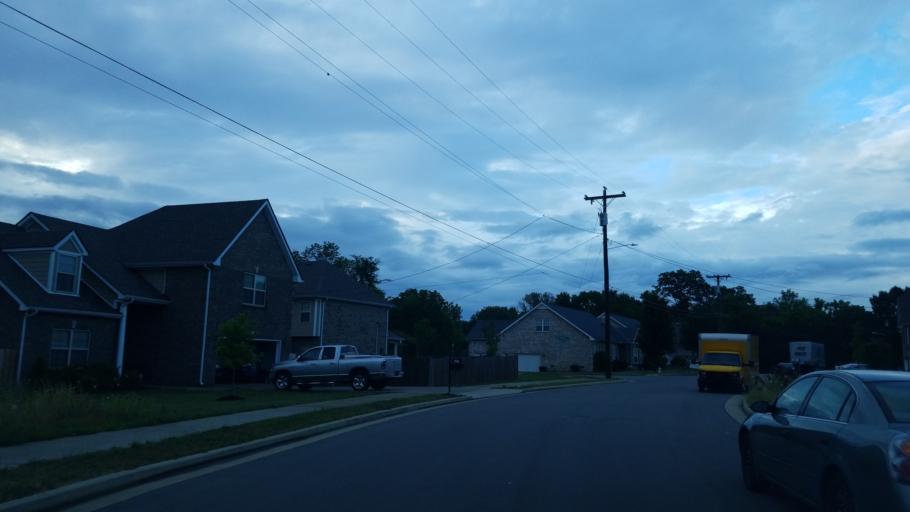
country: US
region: Tennessee
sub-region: Rutherford County
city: La Vergne
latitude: 36.0555
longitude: -86.5913
